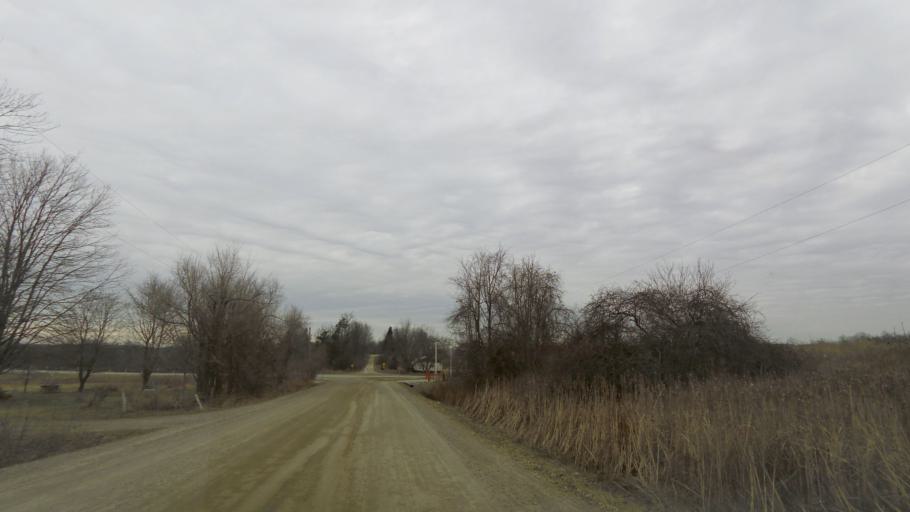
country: CA
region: Ontario
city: Brantford
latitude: 43.0643
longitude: -80.2216
